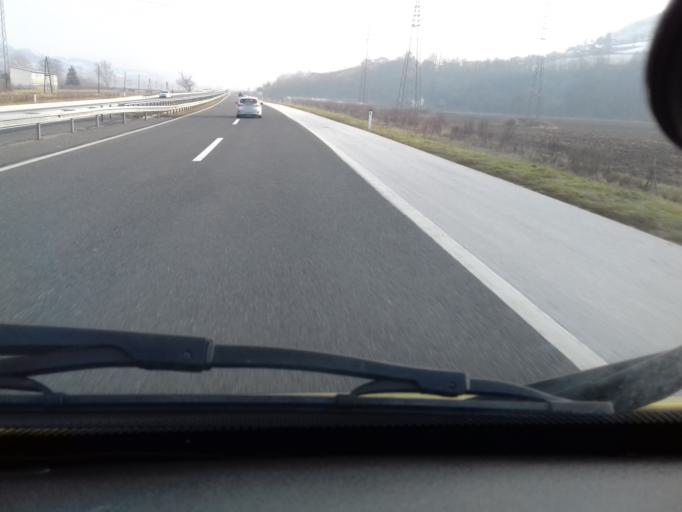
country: BA
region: Federation of Bosnia and Herzegovina
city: Dobrinje
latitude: 44.0499
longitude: 18.1085
